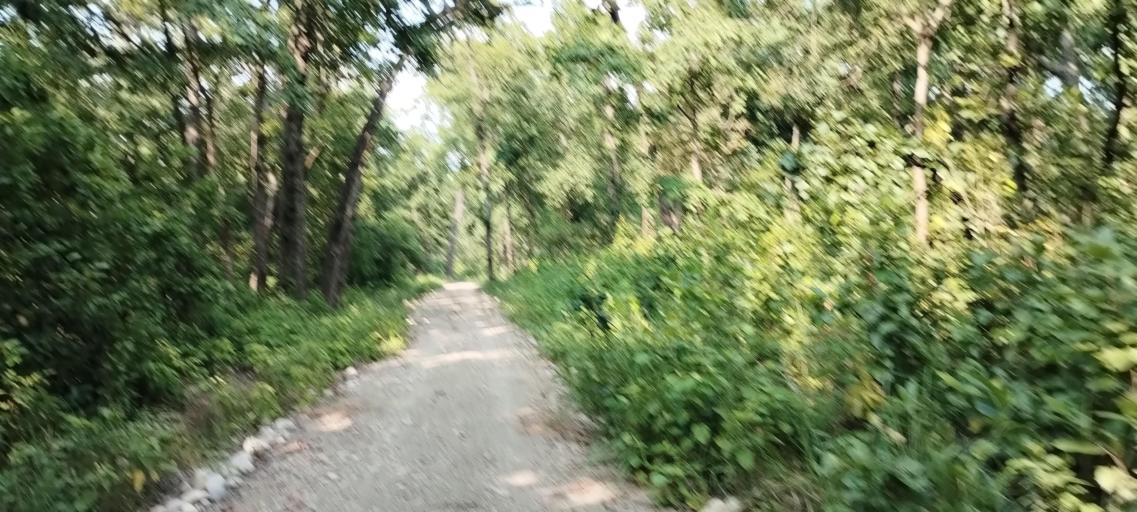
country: NP
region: Far Western
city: Tikapur
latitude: 28.5634
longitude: 81.2665
